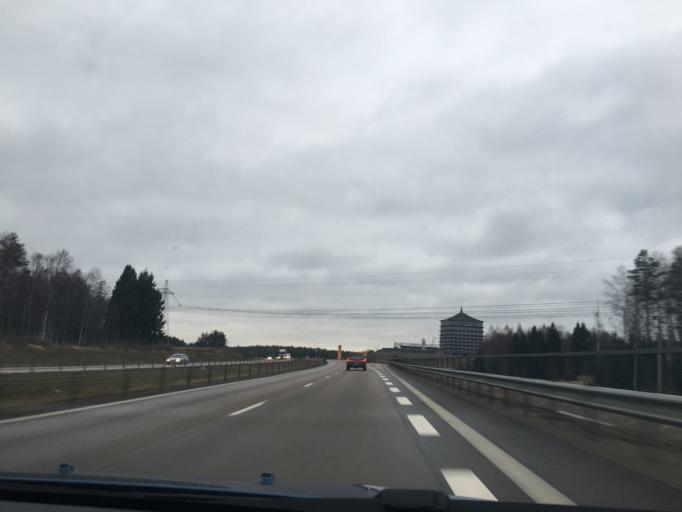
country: SE
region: Uppsala
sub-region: Alvkarleby Kommun
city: AElvkarleby
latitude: 60.4583
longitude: 17.4151
